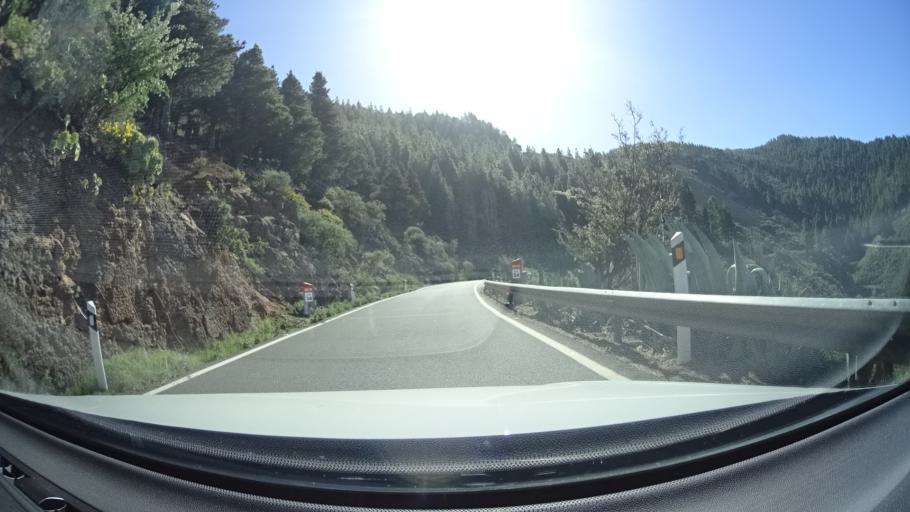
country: ES
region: Canary Islands
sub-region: Provincia de Las Palmas
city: Artenara
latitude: 28.0294
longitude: -15.6192
